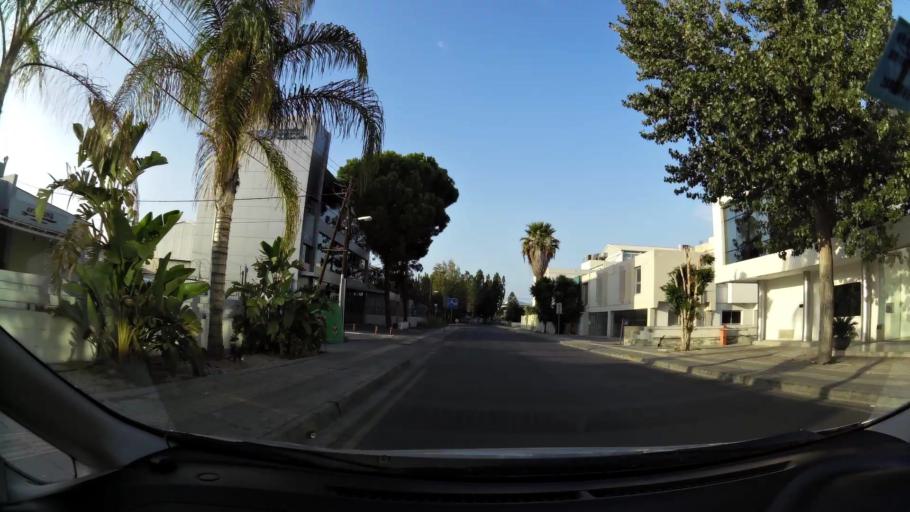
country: CY
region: Lefkosia
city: Nicosia
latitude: 35.1653
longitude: 33.3243
